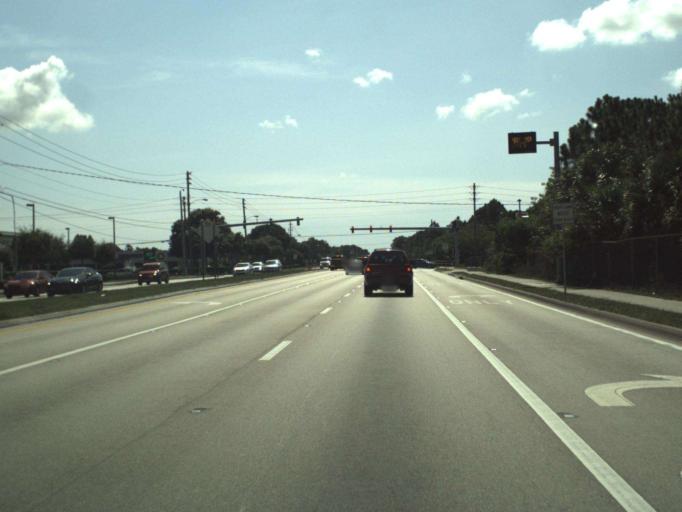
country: US
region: Florida
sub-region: Brevard County
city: June Park
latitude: 28.1206
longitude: -80.7018
